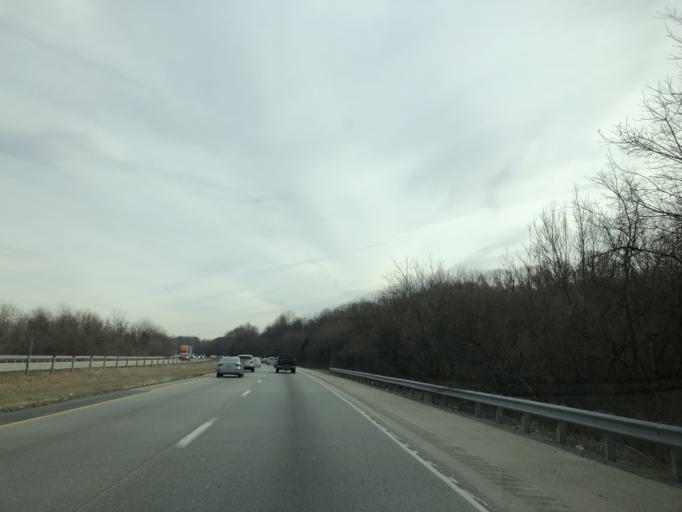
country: US
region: Pennsylvania
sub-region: Chester County
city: Exton
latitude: 40.0130
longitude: -75.6469
